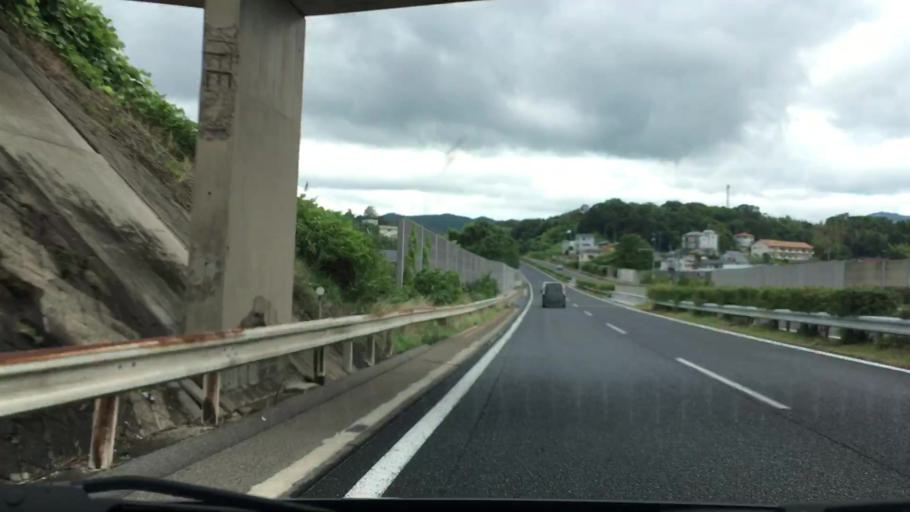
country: JP
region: Okayama
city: Tsuyama
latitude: 35.0749
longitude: 134.0201
